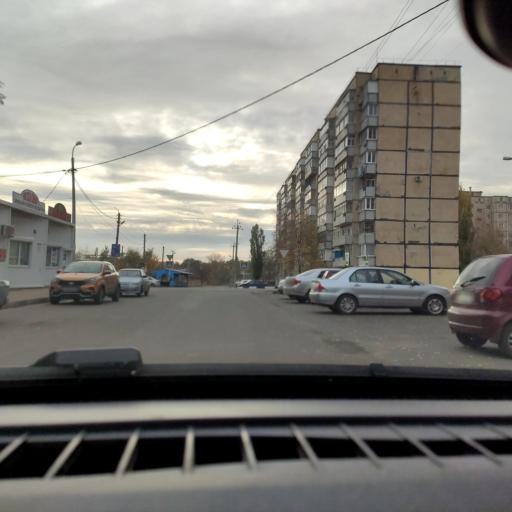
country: RU
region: Belgorod
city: Alekseyevka
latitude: 50.6291
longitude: 38.7006
